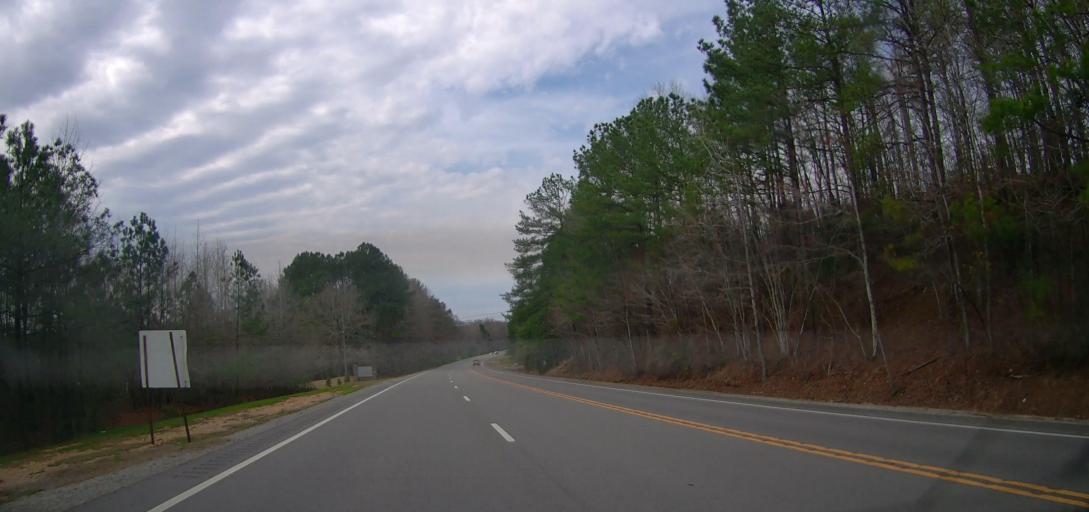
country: US
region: Alabama
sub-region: Marion County
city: Guin
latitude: 33.9900
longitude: -87.9254
